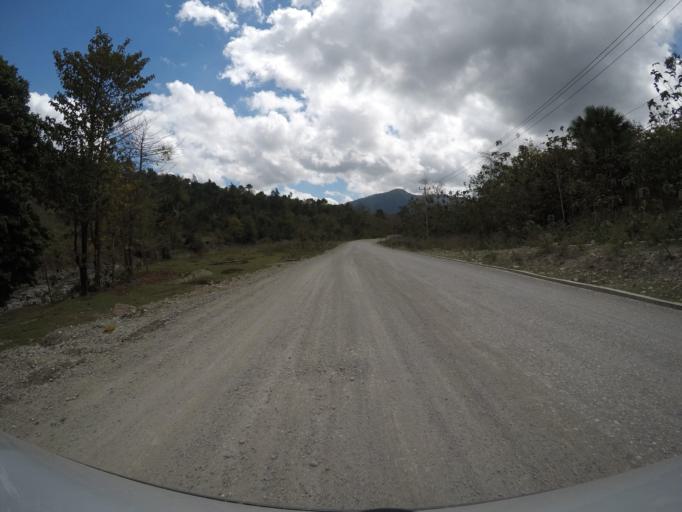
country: TL
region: Viqueque
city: Viqueque
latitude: -8.8182
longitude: 126.3790
